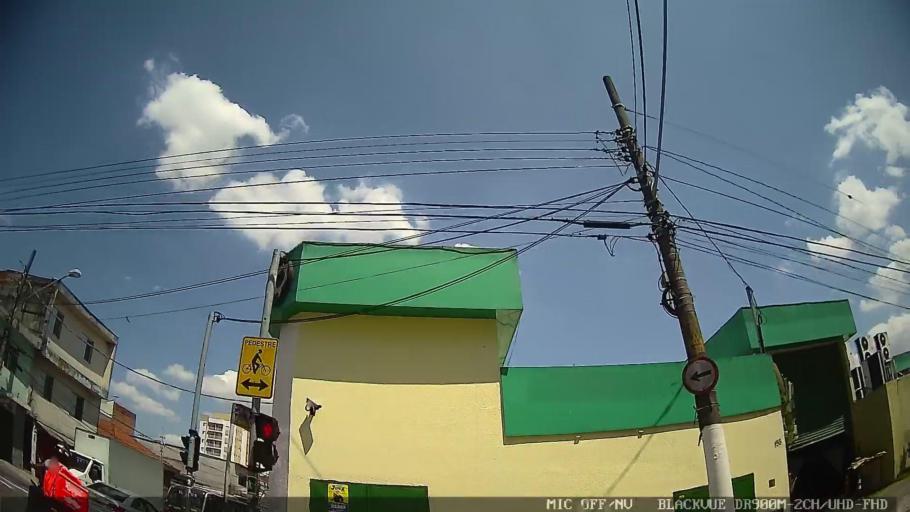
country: BR
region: Sao Paulo
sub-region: Guarulhos
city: Guarulhos
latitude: -23.5151
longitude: -46.4981
